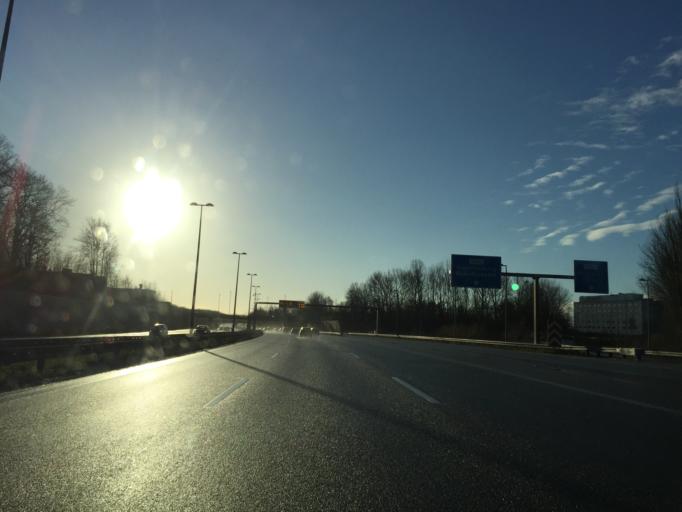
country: DK
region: Capital Region
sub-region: Glostrup Kommune
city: Glostrup
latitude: 55.6711
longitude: 12.4222
